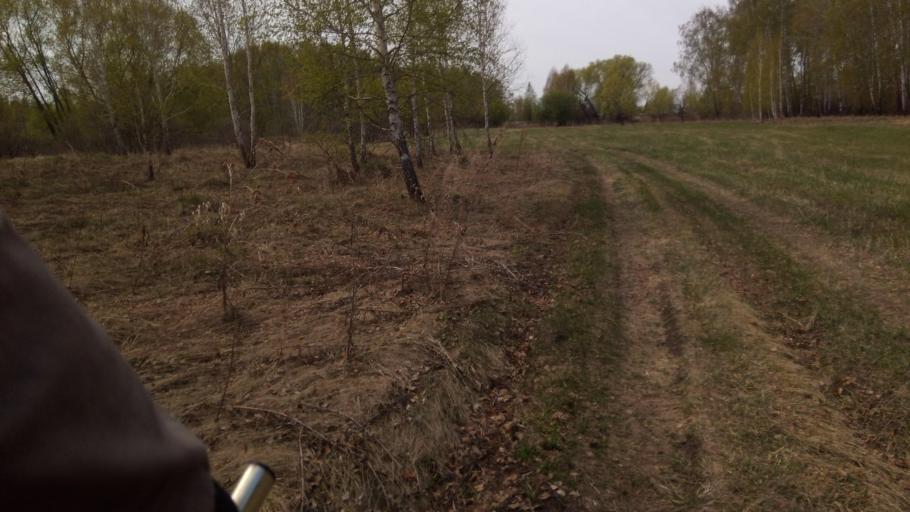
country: RU
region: Chelyabinsk
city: Timiryazevskiy
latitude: 55.0024
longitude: 60.8505
